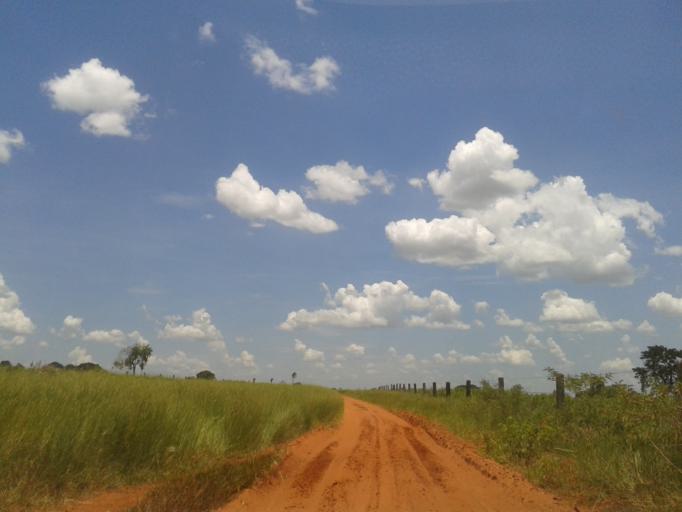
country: BR
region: Minas Gerais
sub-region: Santa Vitoria
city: Santa Vitoria
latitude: -19.2139
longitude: -50.4165
